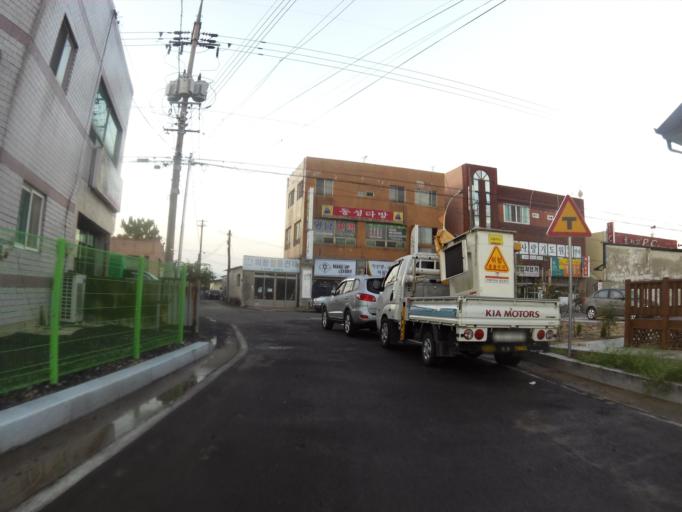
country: KR
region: Gyeongsangnam-do
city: Naeso
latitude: 35.3889
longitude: 128.4757
